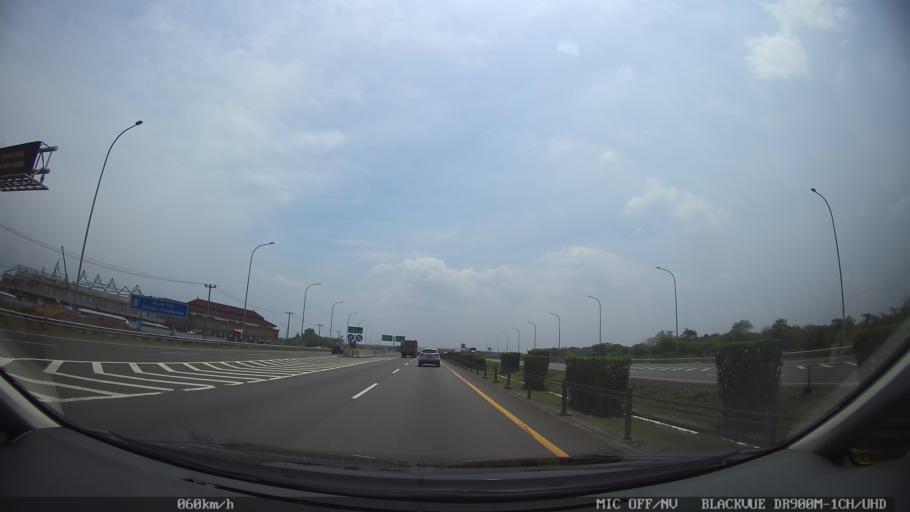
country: ID
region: Banten
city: Serang
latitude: -6.1388
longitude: 106.2524
